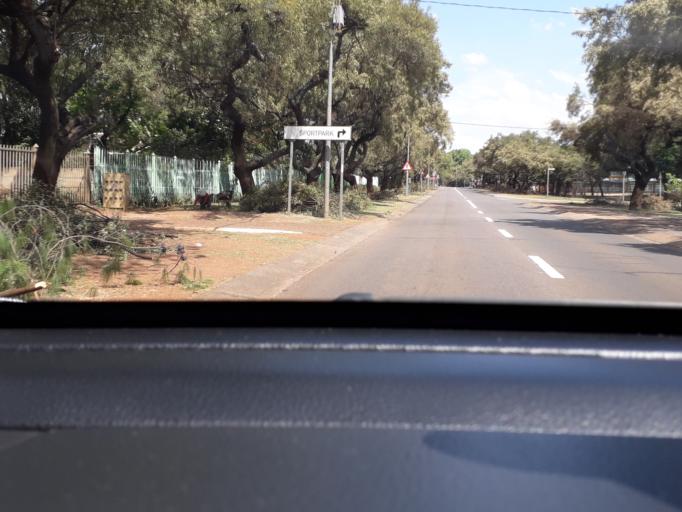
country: ZA
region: Gauteng
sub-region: City of Tshwane Metropolitan Municipality
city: Centurion
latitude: -25.8244
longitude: 28.2081
